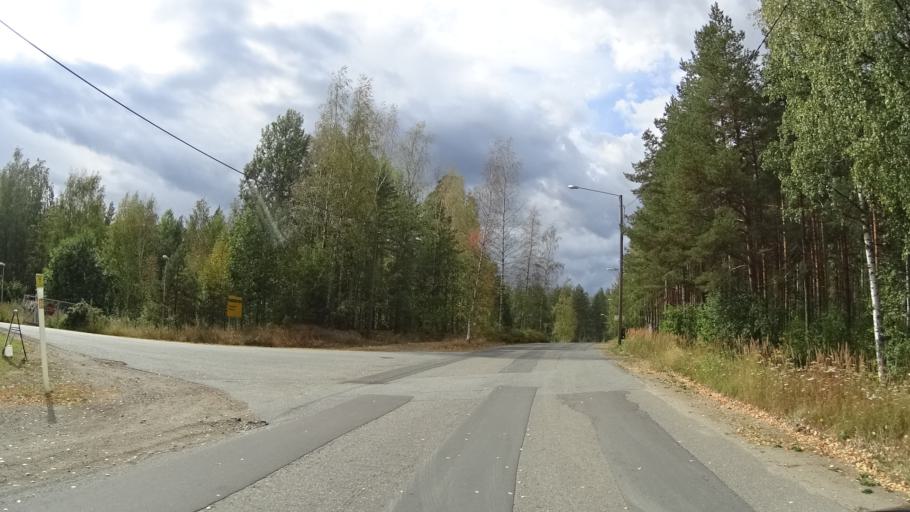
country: FI
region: Pirkanmaa
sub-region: Tampere
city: Kangasala
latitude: 61.4454
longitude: 24.1263
